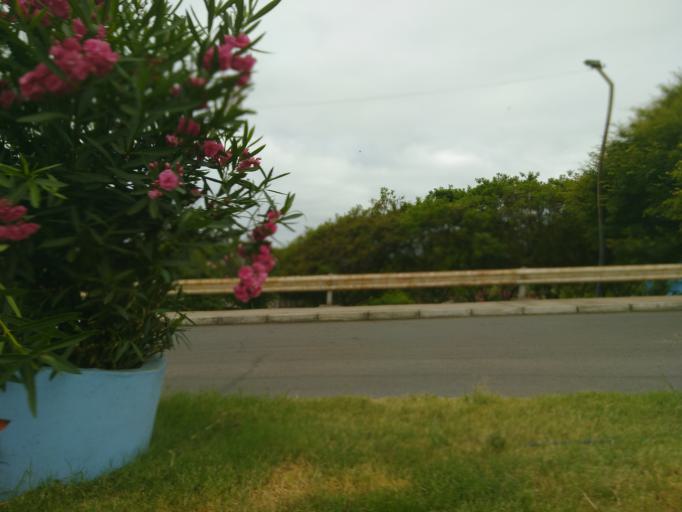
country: CL
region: Antofagasta
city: Taltal
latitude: -25.4051
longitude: -70.4818
